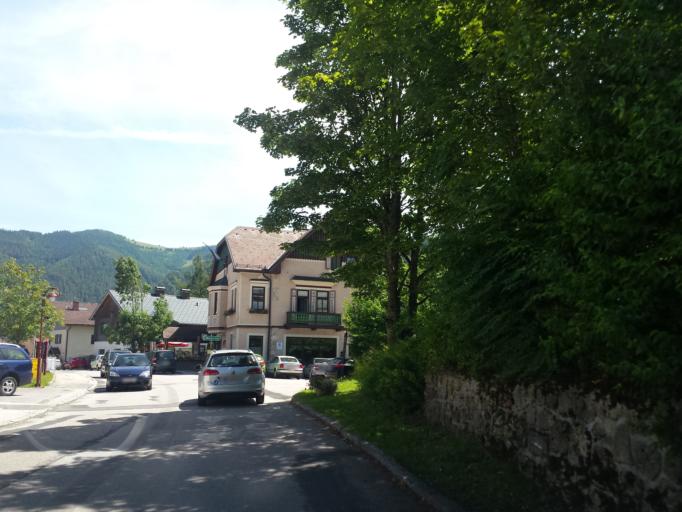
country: AT
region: Lower Austria
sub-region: Politischer Bezirk Neunkirchen
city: Semmering
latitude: 47.6352
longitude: 15.8275
